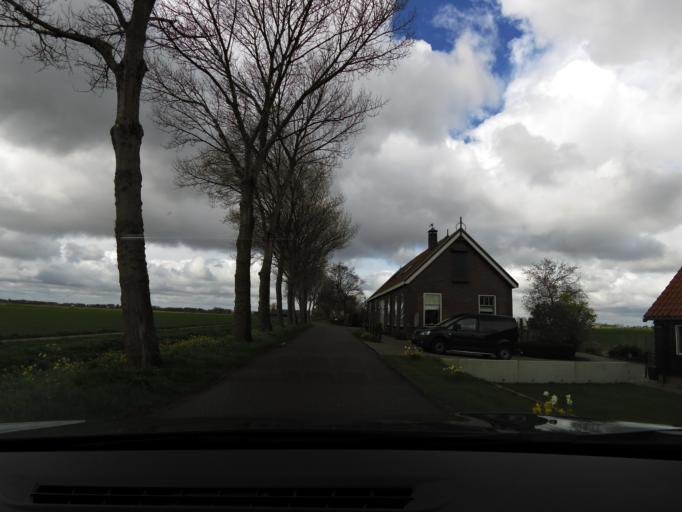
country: NL
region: South Holland
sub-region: Gemeente Brielle
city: Brielle
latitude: 51.8540
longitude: 4.2164
